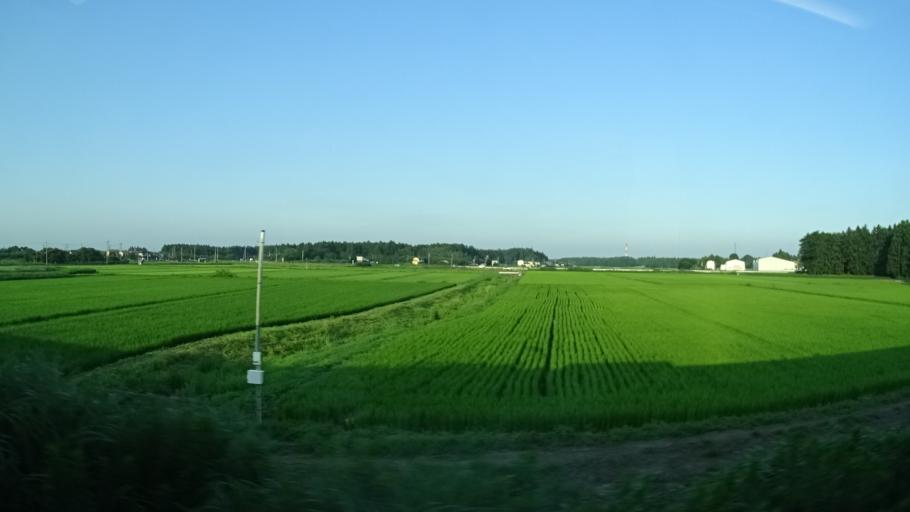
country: JP
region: Ibaraki
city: Tomobe
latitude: 36.2708
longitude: 140.2811
